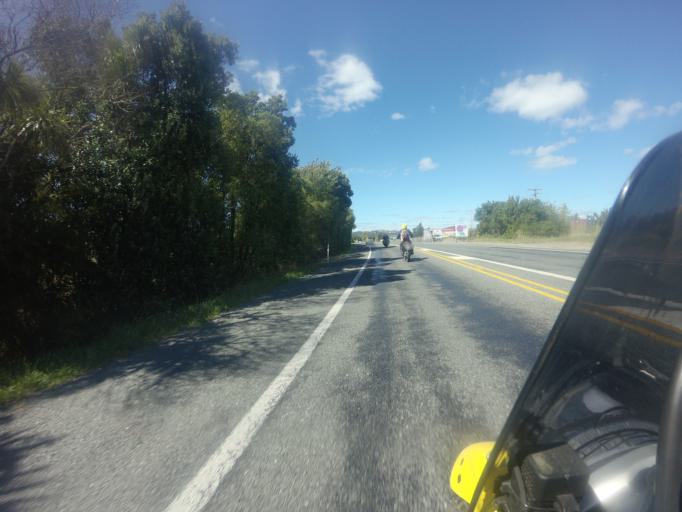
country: NZ
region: Bay of Plenty
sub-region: Whakatane District
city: Whakatane
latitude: -37.9513
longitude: 176.9514
